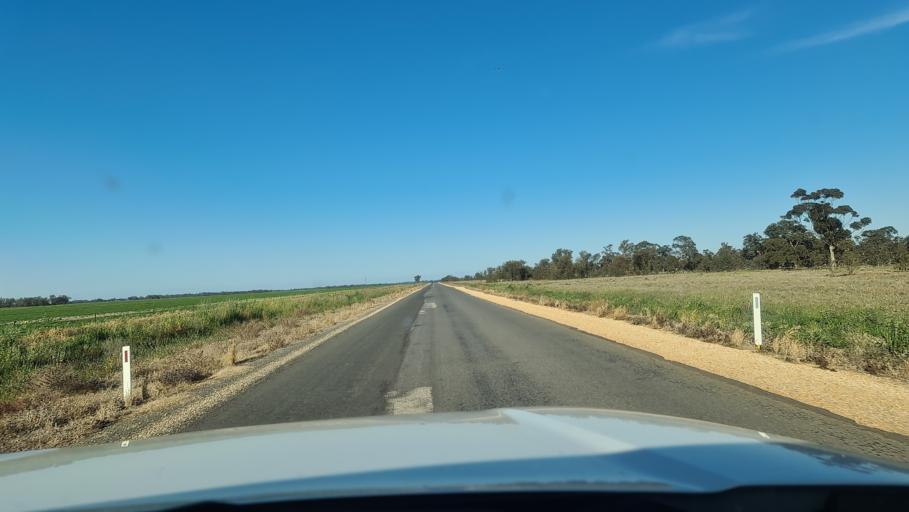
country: AU
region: Victoria
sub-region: Horsham
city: Horsham
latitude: -36.4492
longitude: 142.5497
